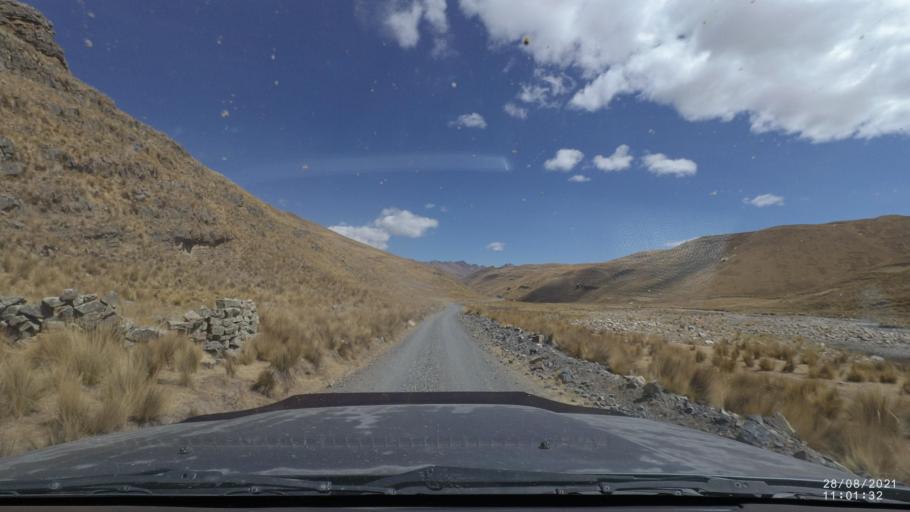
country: BO
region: Cochabamba
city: Cochabamba
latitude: -17.1806
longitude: -66.2671
